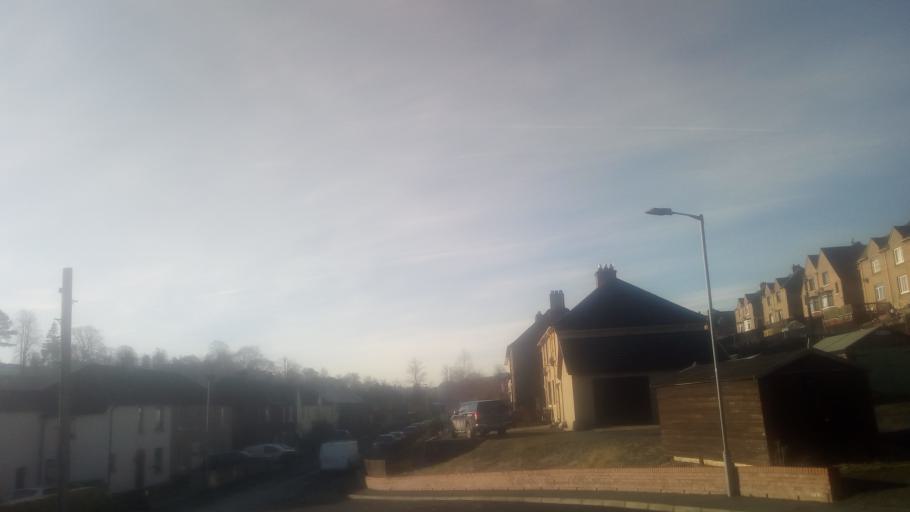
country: GB
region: Scotland
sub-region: The Scottish Borders
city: Jedburgh
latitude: 55.4816
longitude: -2.5470
